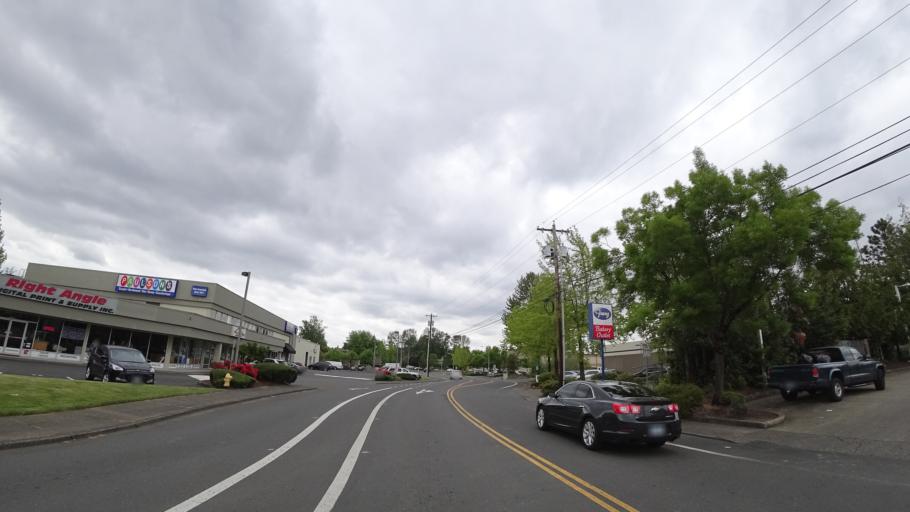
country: US
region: Oregon
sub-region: Washington County
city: Tigard
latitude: 45.4417
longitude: -122.7793
